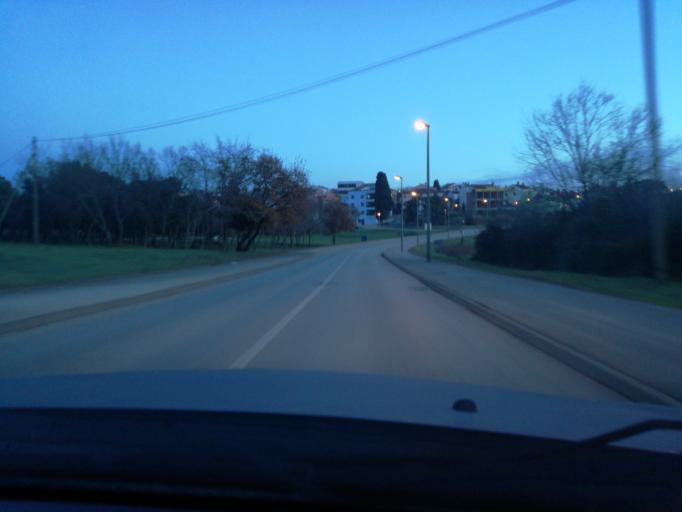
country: HR
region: Istarska
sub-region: Grad Rovinj
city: Rovinj
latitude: 45.0921
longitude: 13.6449
